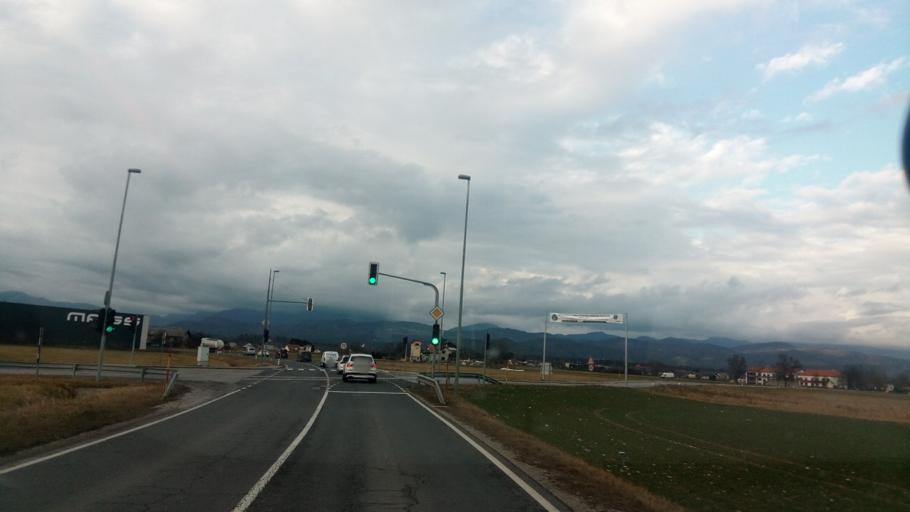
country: SI
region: Domzale
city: Vir
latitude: 46.1462
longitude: 14.6173
